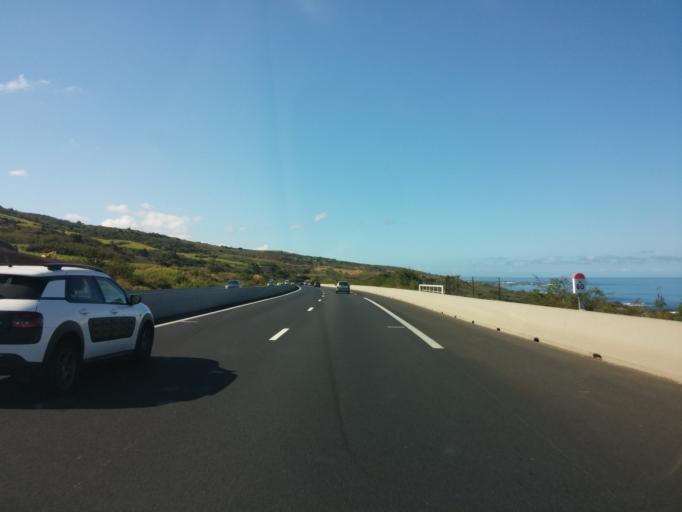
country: RE
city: Piton Saint-Leu
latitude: -21.2265
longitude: 55.3055
